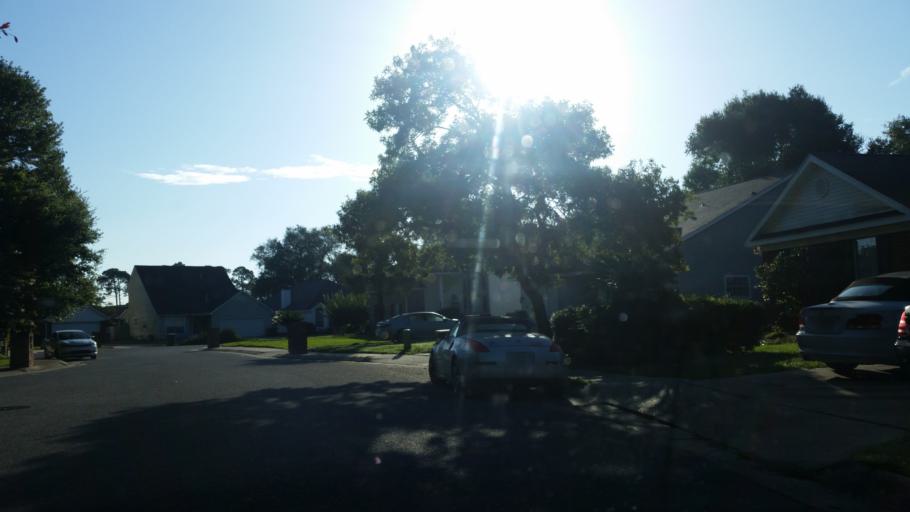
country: US
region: Florida
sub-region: Escambia County
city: Ferry Pass
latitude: 30.5052
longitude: -87.1683
